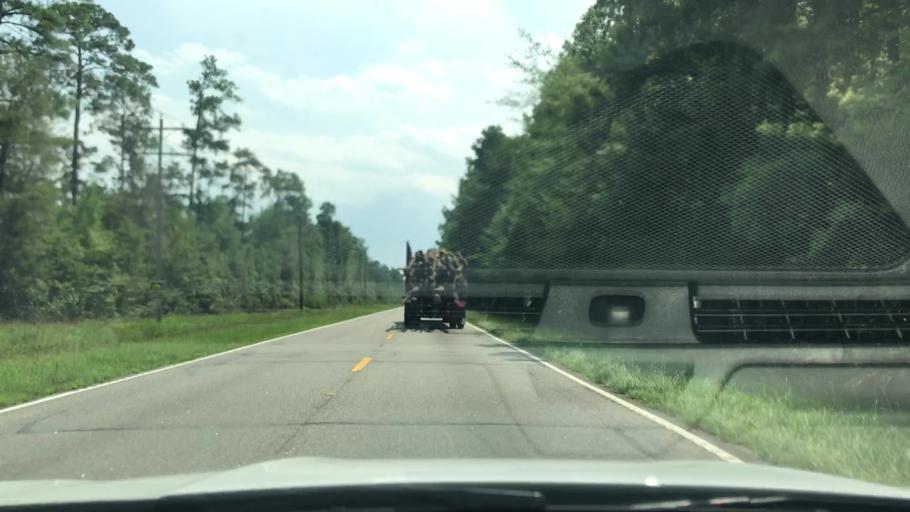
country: US
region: South Carolina
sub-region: Georgetown County
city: Georgetown
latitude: 33.4489
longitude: -79.2789
